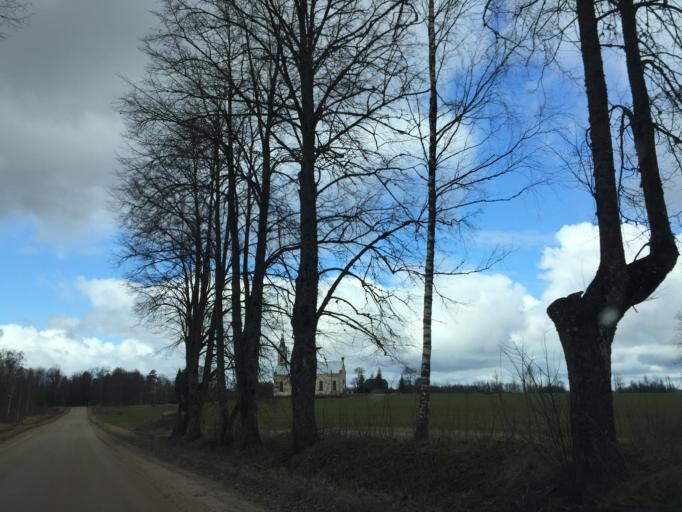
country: LV
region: Akniste
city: Akniste
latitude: 56.0854
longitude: 26.0255
